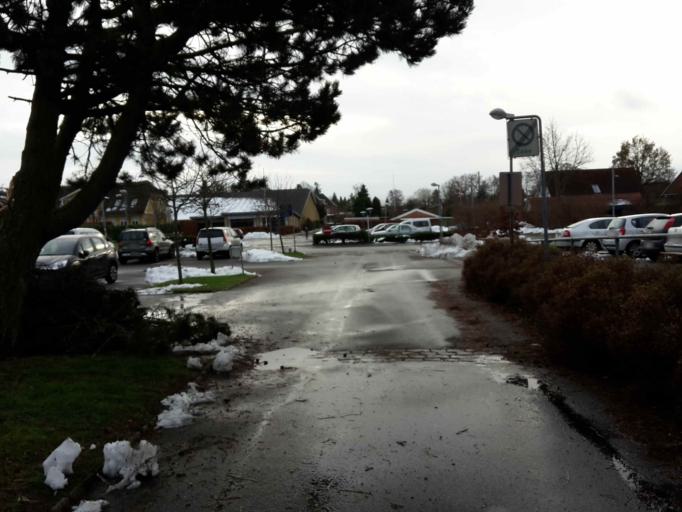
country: DK
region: Capital Region
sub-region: Allerod Kommune
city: Blovstrod
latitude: 55.8686
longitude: 12.3863
